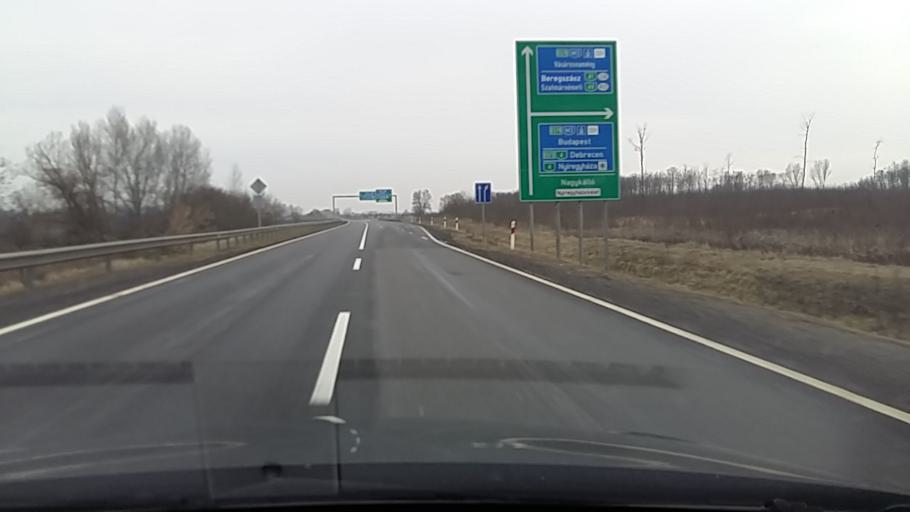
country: HU
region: Szabolcs-Szatmar-Bereg
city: Nagykallo
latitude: 47.9039
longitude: 21.8175
